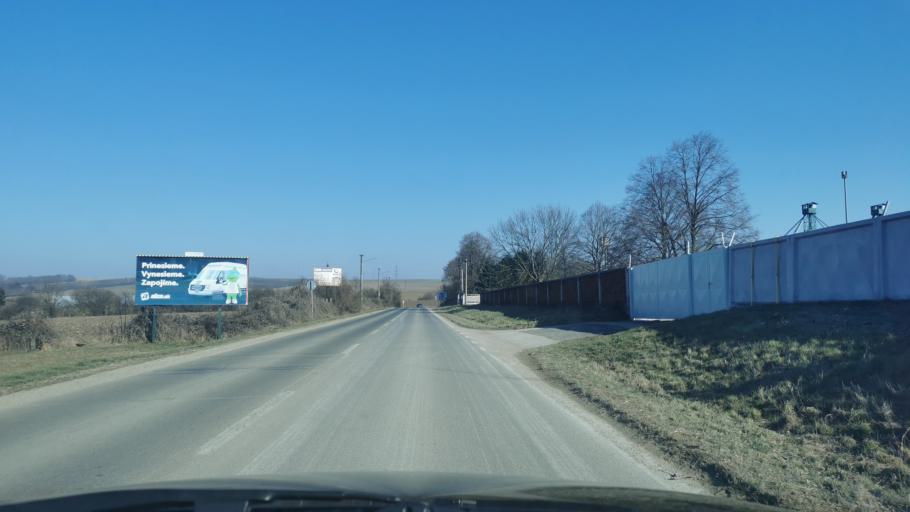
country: SK
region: Trnavsky
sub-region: Okres Senica
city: Senica
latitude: 48.6816
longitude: 17.3852
